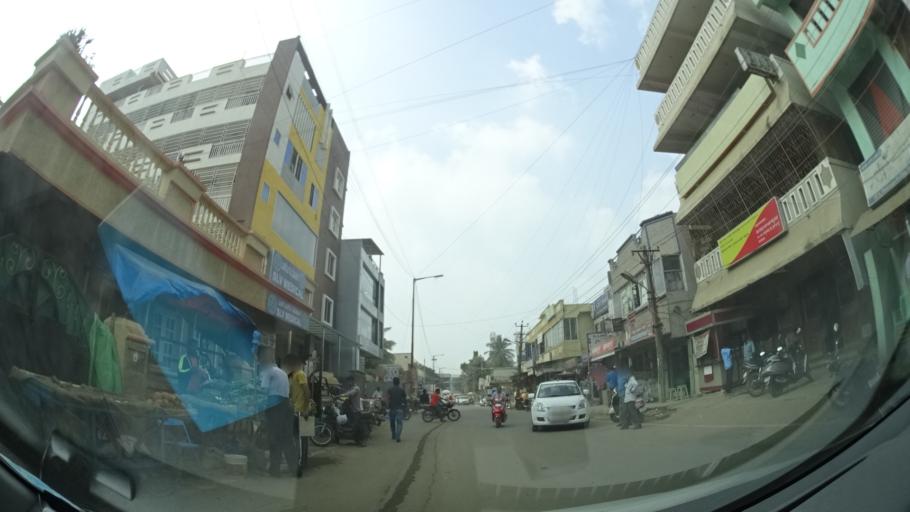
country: IN
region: Karnataka
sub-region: Bangalore Rural
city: Hoskote
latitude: 12.9697
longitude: 77.7518
